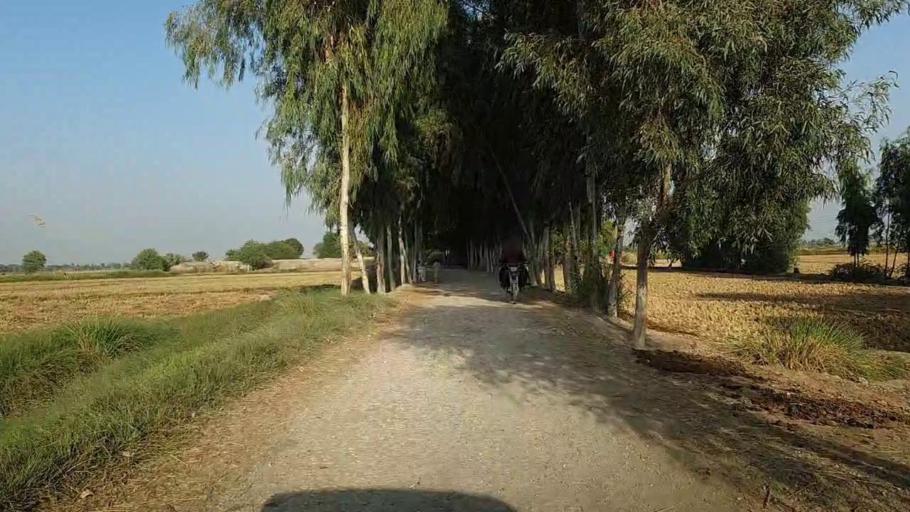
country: PK
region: Sindh
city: Kashmor
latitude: 28.4196
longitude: 69.4160
